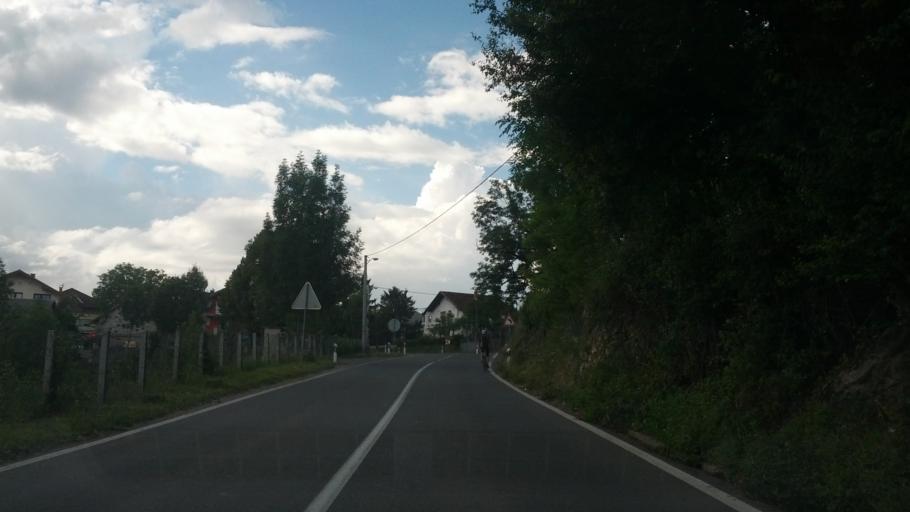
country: BA
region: Federation of Bosnia and Herzegovina
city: Izacic
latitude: 44.8778
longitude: 15.7779
